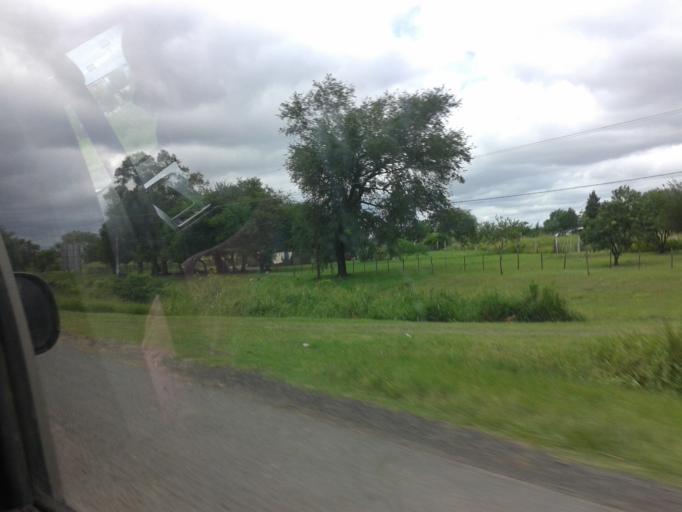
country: AR
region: Formosa
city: Formosa
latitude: -26.1205
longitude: -58.2205
